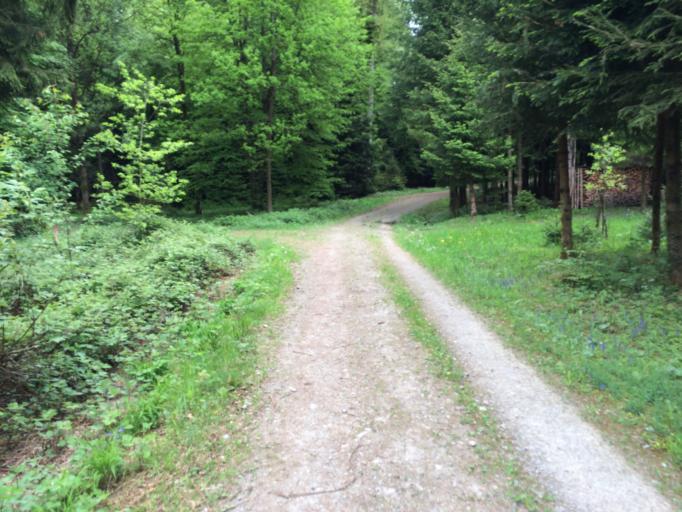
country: CH
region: Zurich
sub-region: Bezirk Uster
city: Uster / Ober-Uster
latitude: 47.3390
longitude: 8.7511
